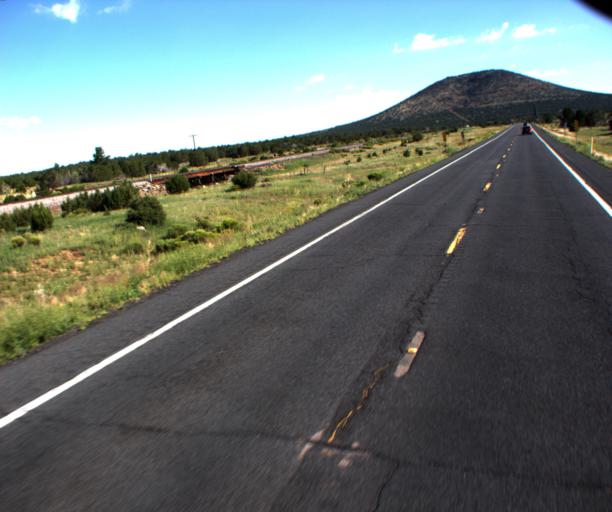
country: US
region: Arizona
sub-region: Coconino County
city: Williams
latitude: 35.3727
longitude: -112.1631
